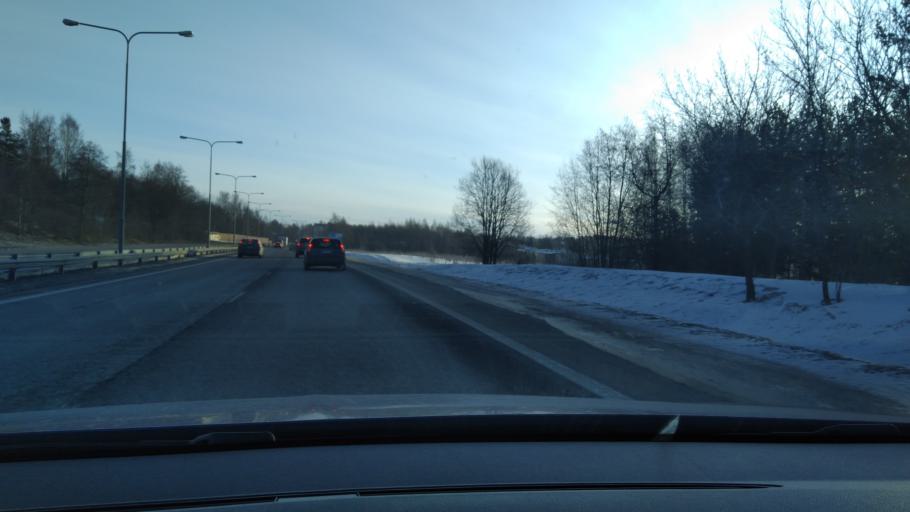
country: FI
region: Pirkanmaa
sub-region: Tampere
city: Pirkkala
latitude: 61.5025
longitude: 23.6773
